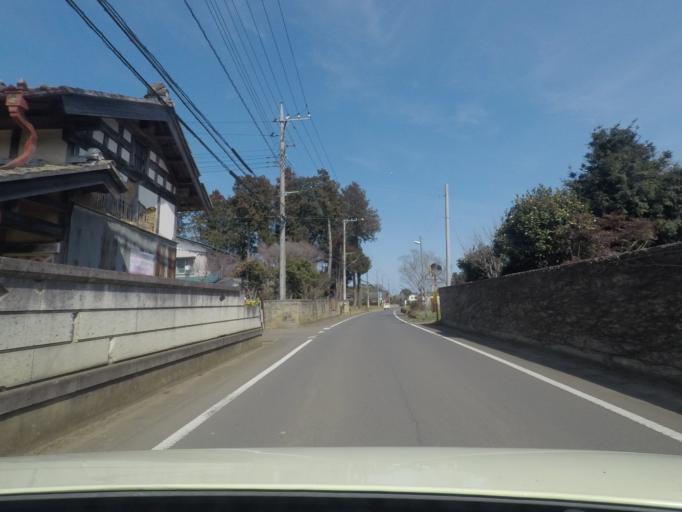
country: JP
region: Ibaraki
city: Okunoya
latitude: 36.2039
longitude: 140.4170
